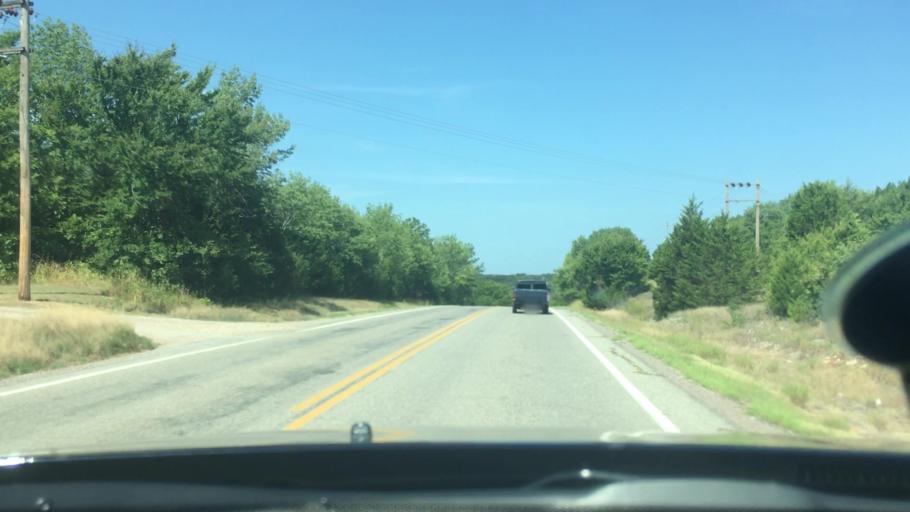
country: US
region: Oklahoma
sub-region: Marshall County
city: Oakland
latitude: 33.9983
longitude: -96.8564
